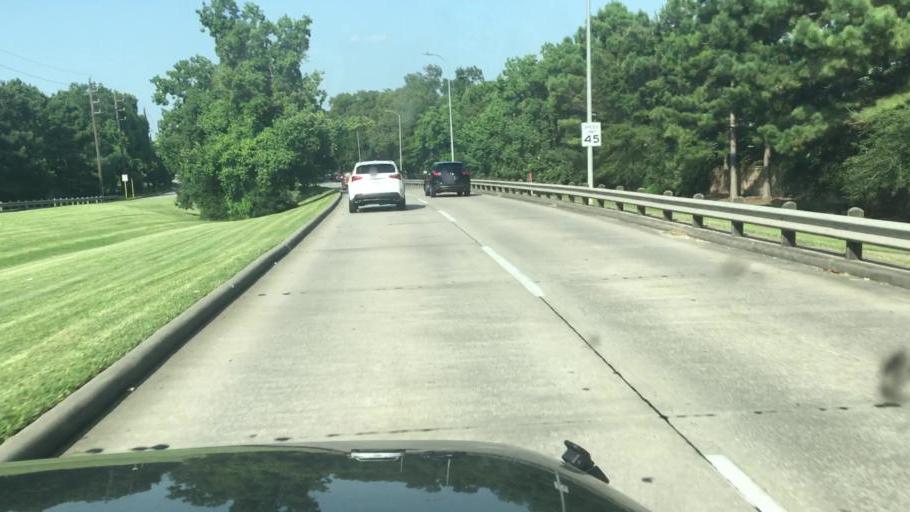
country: US
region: Texas
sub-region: Harris County
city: Atascocita
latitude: 29.9249
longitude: -95.1828
